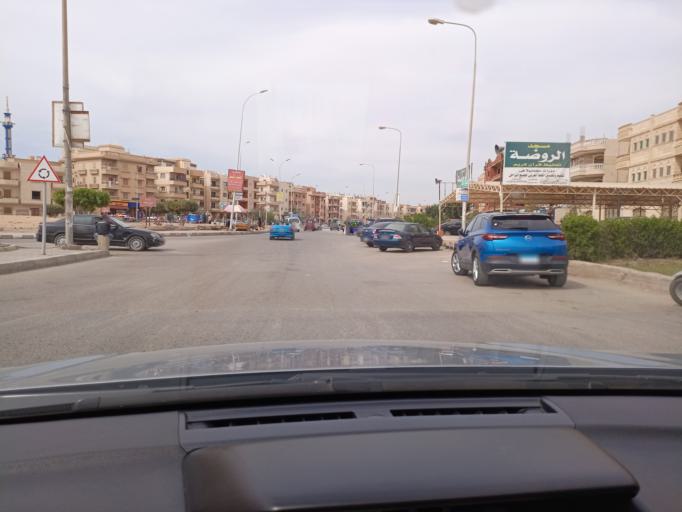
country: EG
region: Muhafazat al Qalyubiyah
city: Al Khankah
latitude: 30.2413
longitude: 31.4820
